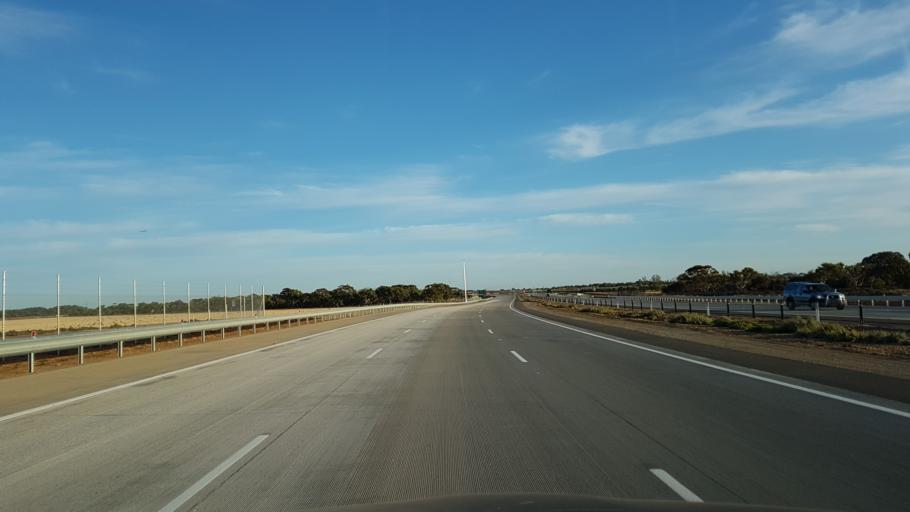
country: AU
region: South Australia
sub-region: Salisbury
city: Salisbury
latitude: -34.7489
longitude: 138.5809
